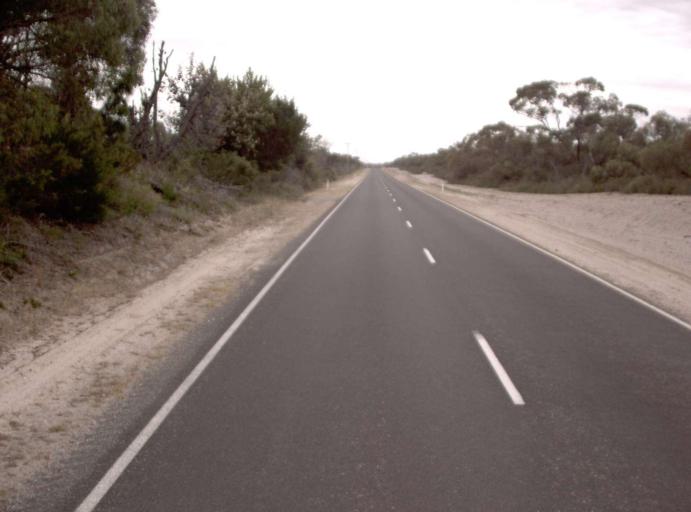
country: AU
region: Victoria
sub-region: Wellington
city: Sale
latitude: -38.1764
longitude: 147.3805
